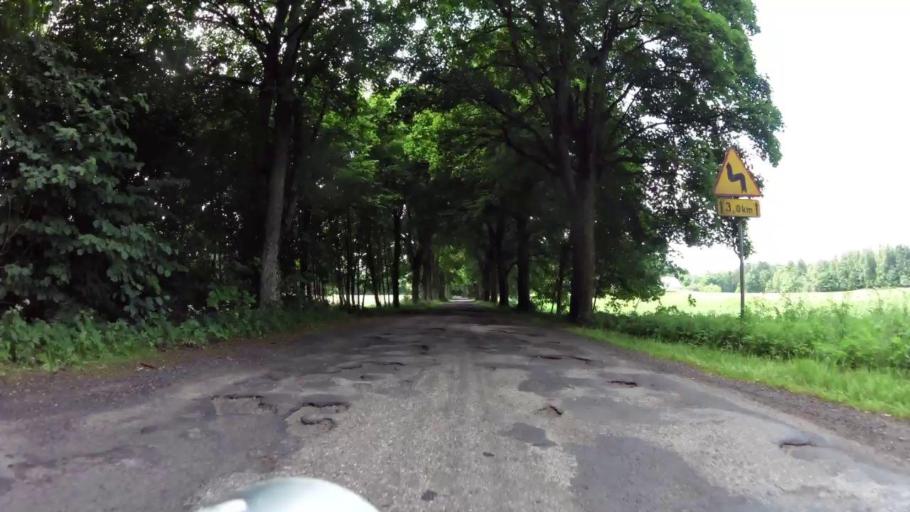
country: PL
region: West Pomeranian Voivodeship
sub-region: Powiat koszalinski
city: Bobolice
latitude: 53.9644
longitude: 16.7164
